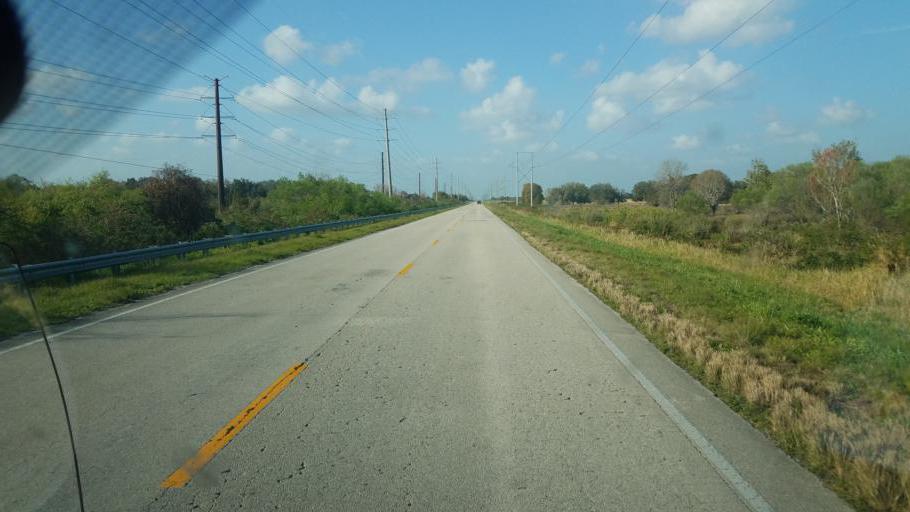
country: US
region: Florida
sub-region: Hardee County
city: Wauchula
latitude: 27.5441
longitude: -81.9304
